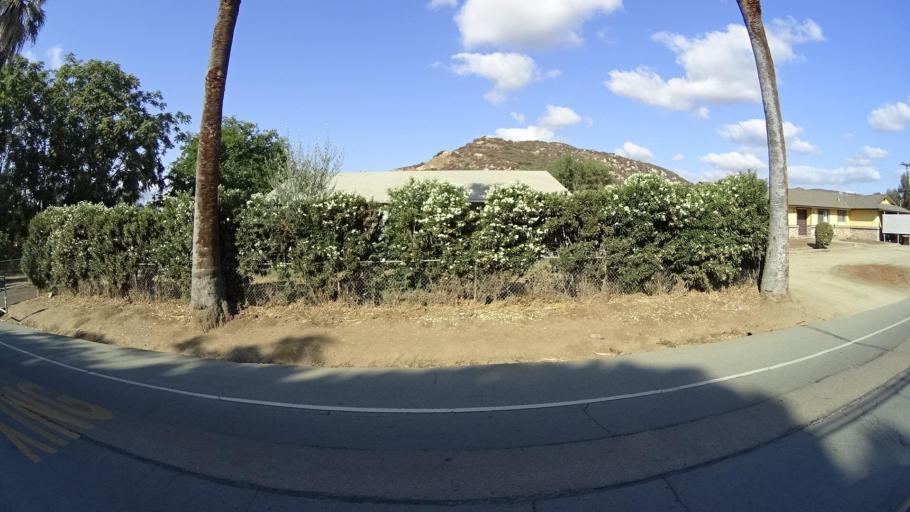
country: US
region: California
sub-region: San Diego County
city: Eucalyptus Hills
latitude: 32.8656
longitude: -116.9430
